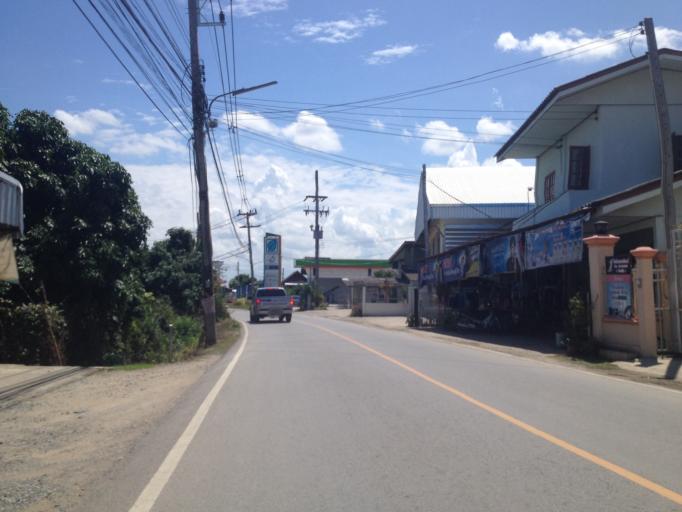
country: TH
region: Chiang Mai
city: Hang Dong
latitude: 18.6597
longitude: 98.9214
